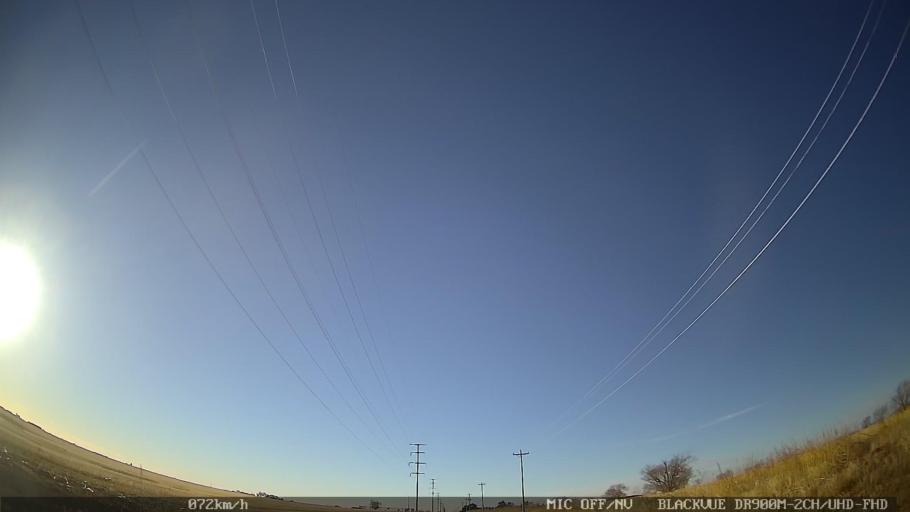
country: US
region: New Mexico
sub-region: Curry County
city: Clovis
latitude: 34.4286
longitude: -103.2493
